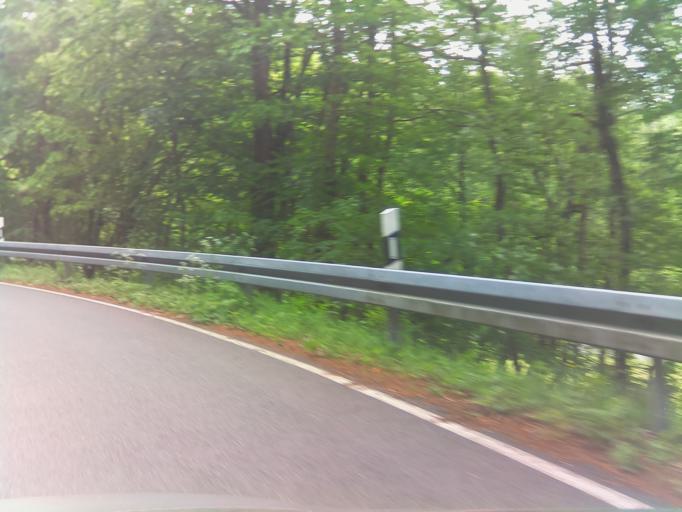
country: DE
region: Bavaria
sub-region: Regierungsbezirk Unterfranken
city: Frammersbach
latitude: 50.1433
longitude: 9.4876
